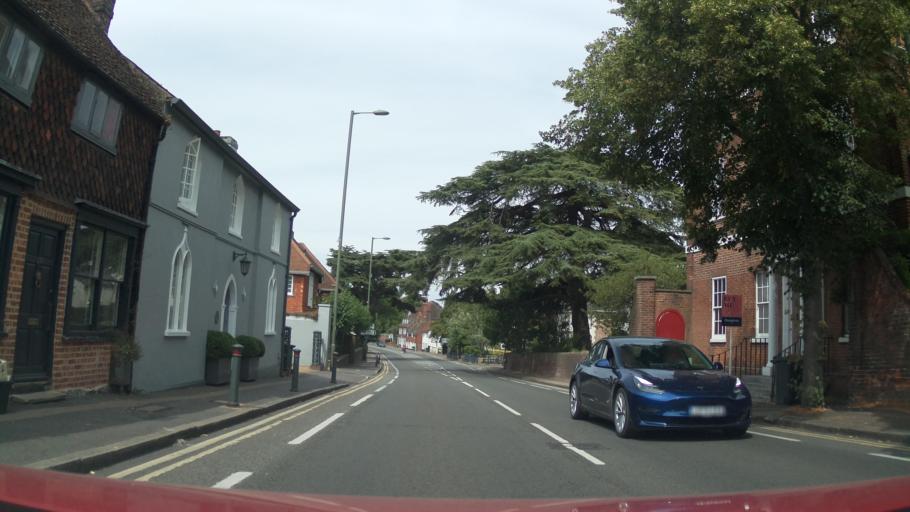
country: GB
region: England
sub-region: Surrey
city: Reigate
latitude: 51.2388
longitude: -0.2117
